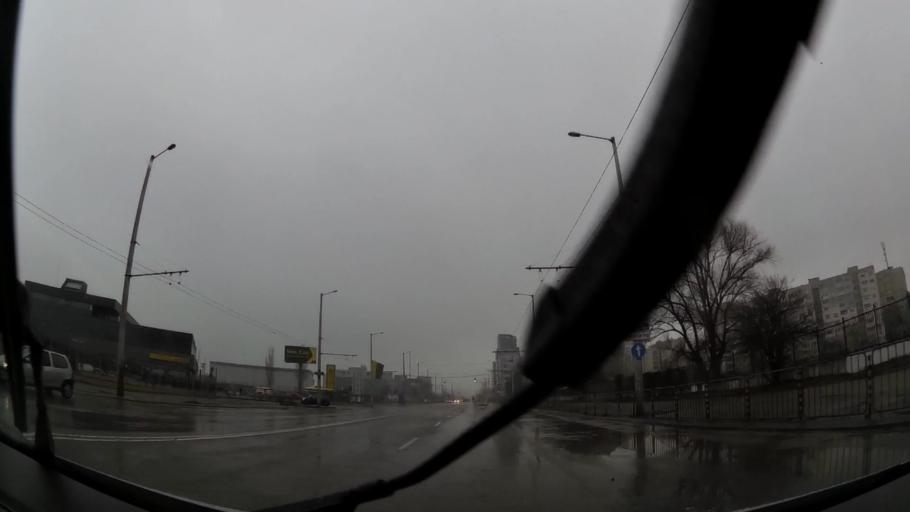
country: BG
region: Sofia-Capital
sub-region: Stolichna Obshtina
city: Sofia
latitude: 42.6533
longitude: 23.4029
